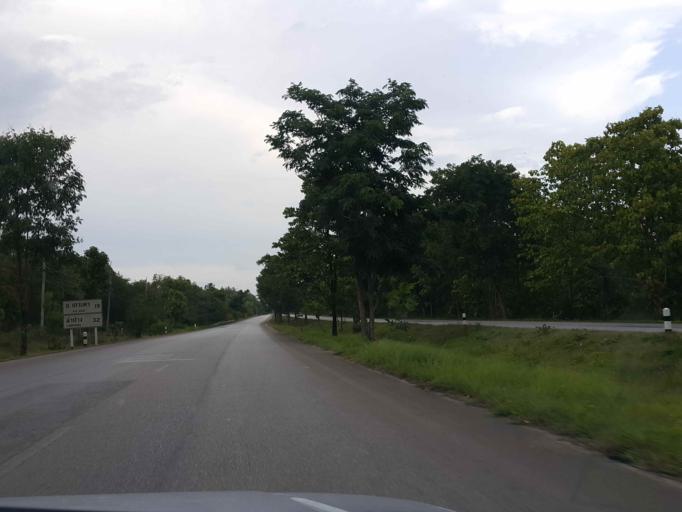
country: TH
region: Lampang
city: Soem Ngam
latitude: 18.0370
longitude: 99.3763
